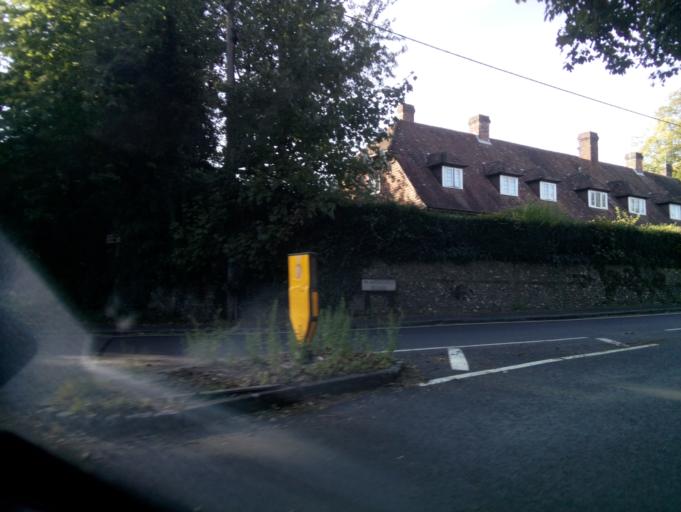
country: GB
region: England
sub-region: Hampshire
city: Swanmore
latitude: 50.9783
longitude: -1.1321
